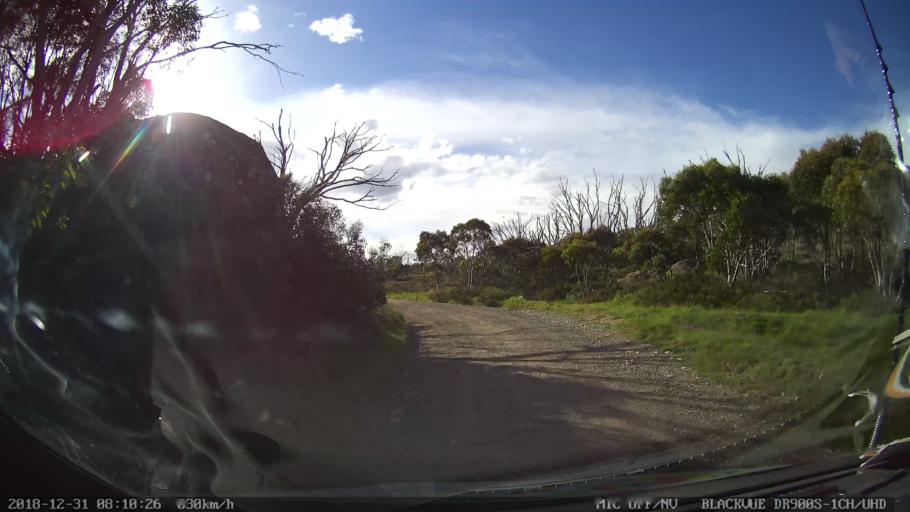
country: AU
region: New South Wales
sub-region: Snowy River
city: Jindabyne
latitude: -36.3830
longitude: 148.4213
